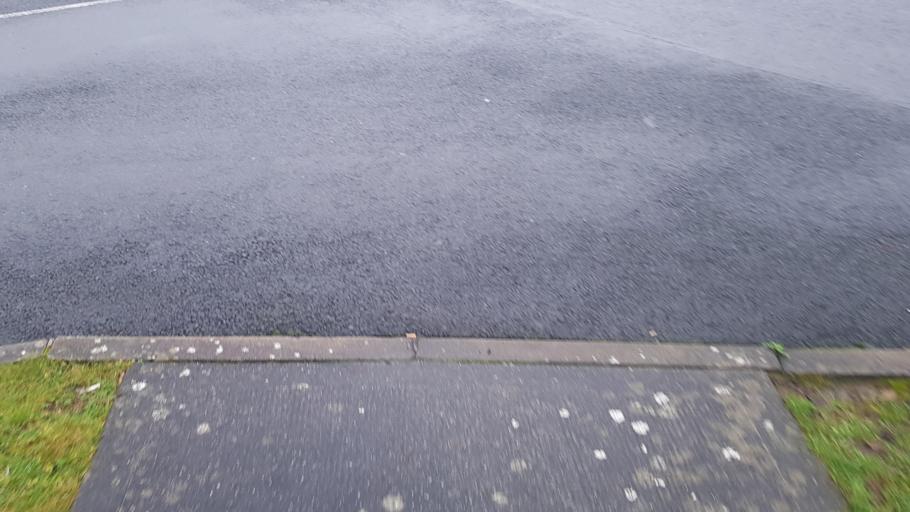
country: IE
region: Connaught
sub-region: County Galway
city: Tuam
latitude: 53.5219
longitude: -8.8515
